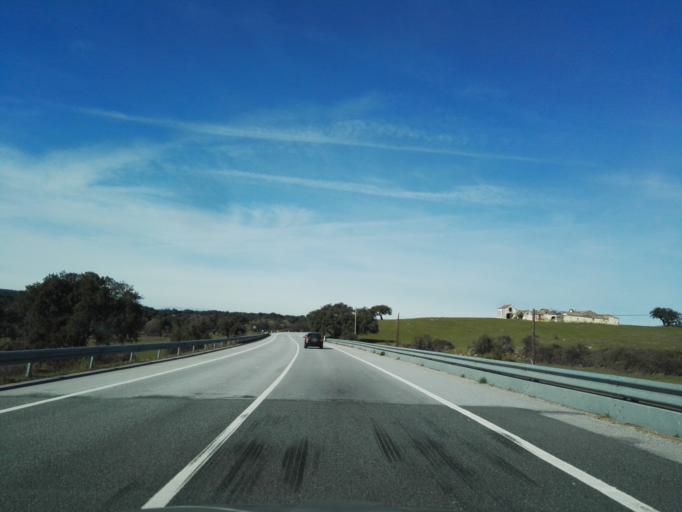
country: PT
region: Portalegre
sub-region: Portalegre
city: Alegrete
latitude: 39.1793
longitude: -7.3420
